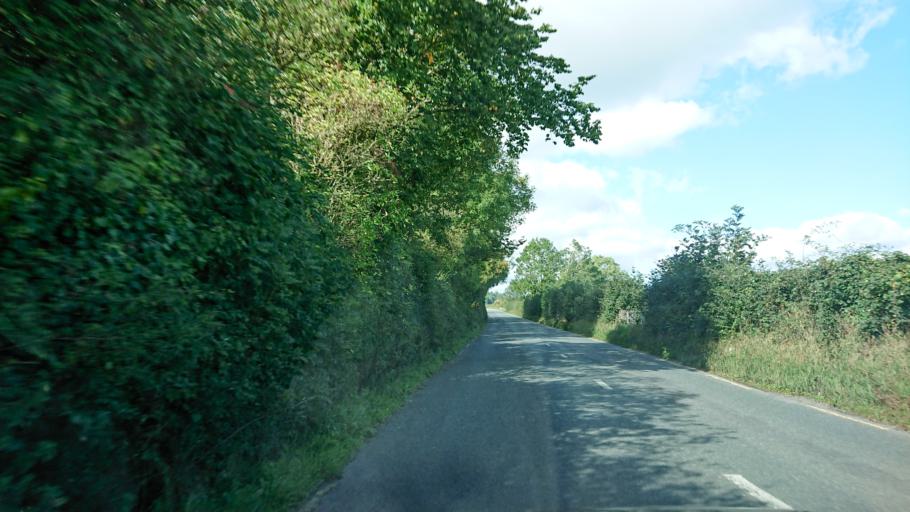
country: IE
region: Munster
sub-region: Waterford
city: Dungarvan
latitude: 52.1144
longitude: -7.6806
